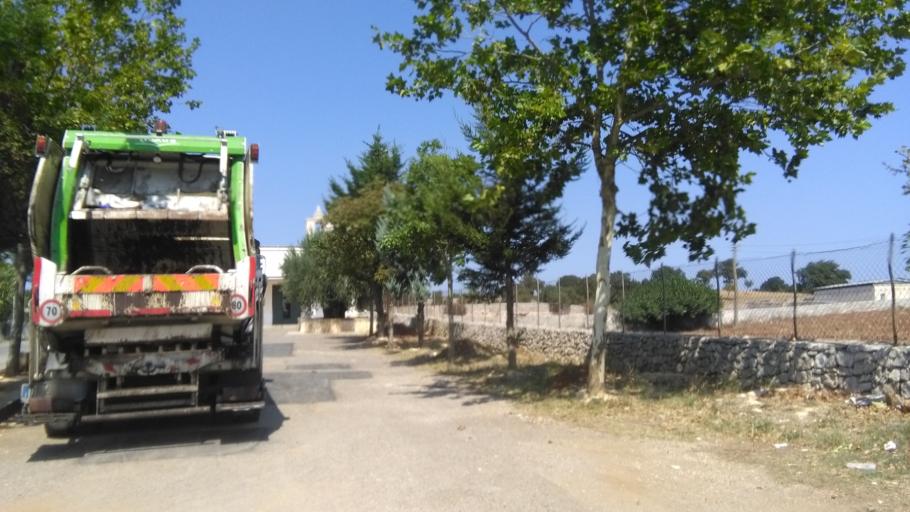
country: IT
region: Apulia
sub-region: Provincia di Brindisi
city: Cisternino
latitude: 40.7028
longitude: 17.4221
